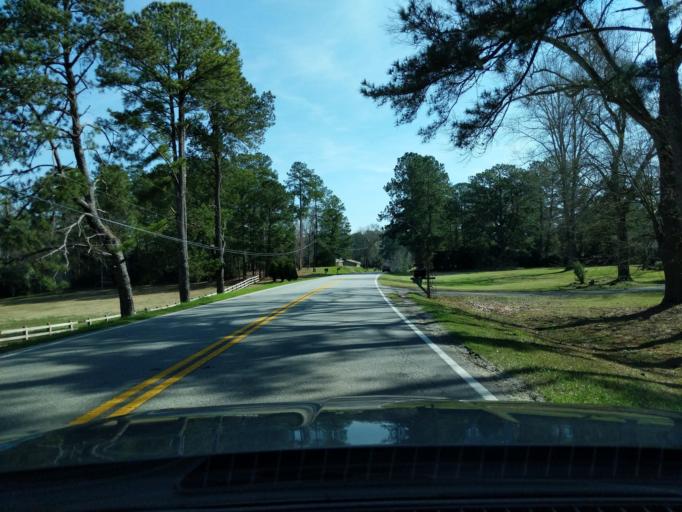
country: US
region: Georgia
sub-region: Columbia County
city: Evans
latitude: 33.5329
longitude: -82.1409
